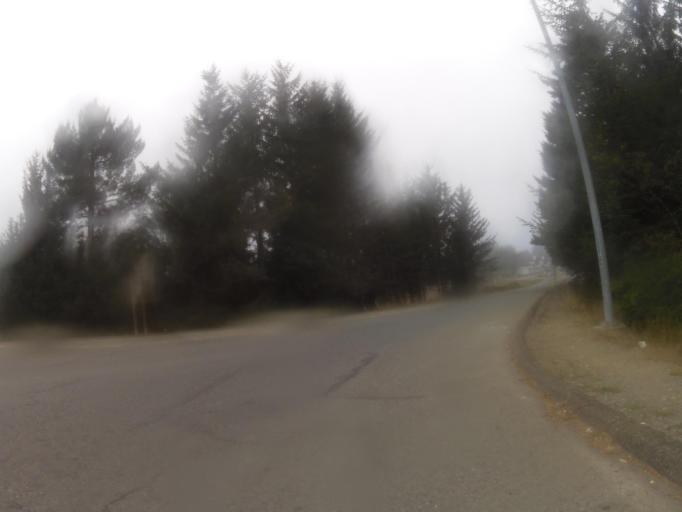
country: US
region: California
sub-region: Del Norte County
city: Crescent City
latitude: 41.7728
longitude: -124.1887
